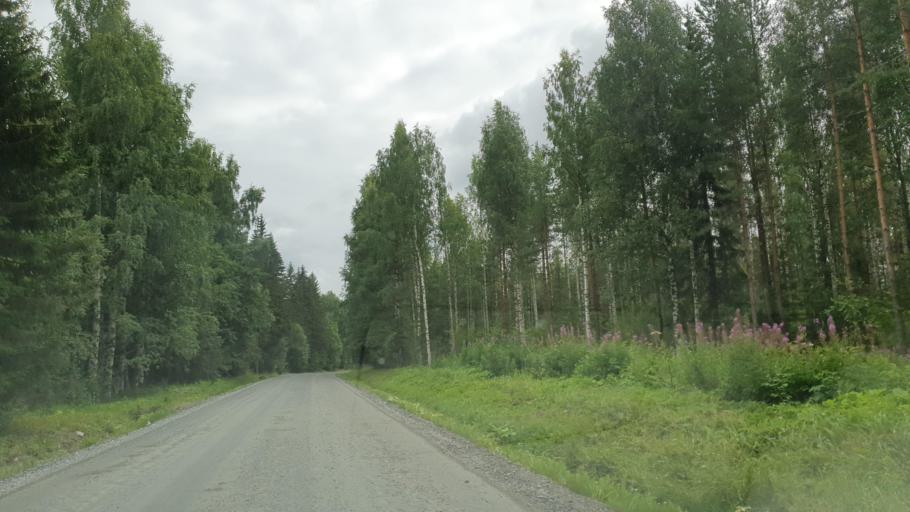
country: FI
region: Northern Savo
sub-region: Ylae-Savo
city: Iisalmi
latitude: 63.5325
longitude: 27.0882
